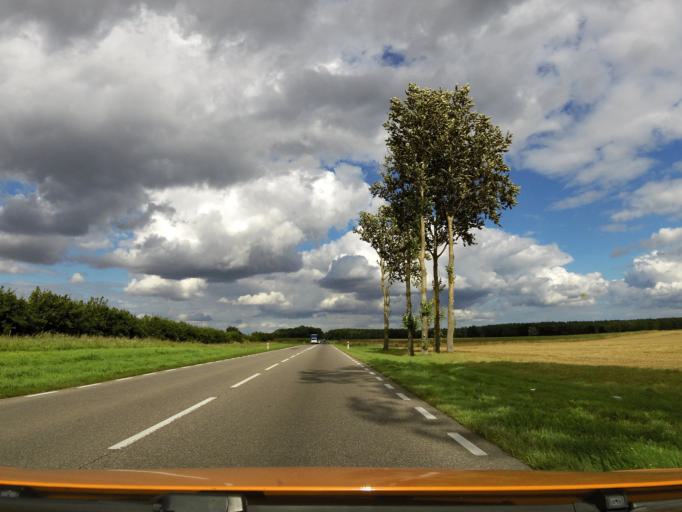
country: PL
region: West Pomeranian Voivodeship
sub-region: Powiat gryficki
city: Brojce
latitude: 53.8849
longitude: 15.4021
